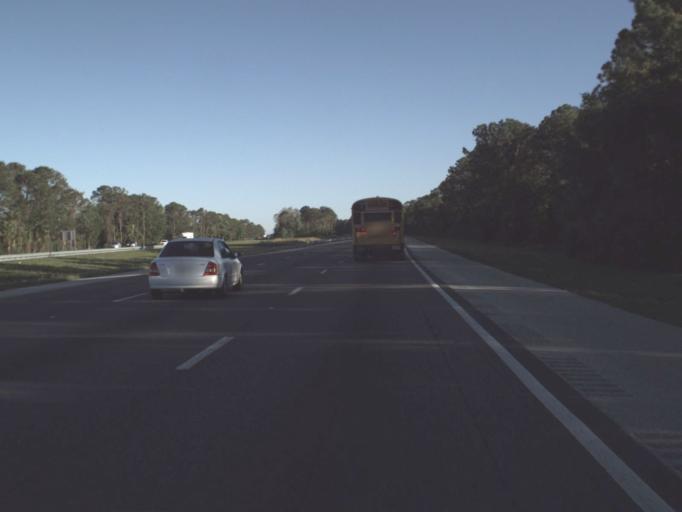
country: US
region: Florida
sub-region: Flagler County
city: Flagler Beach
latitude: 29.4369
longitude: -81.1692
